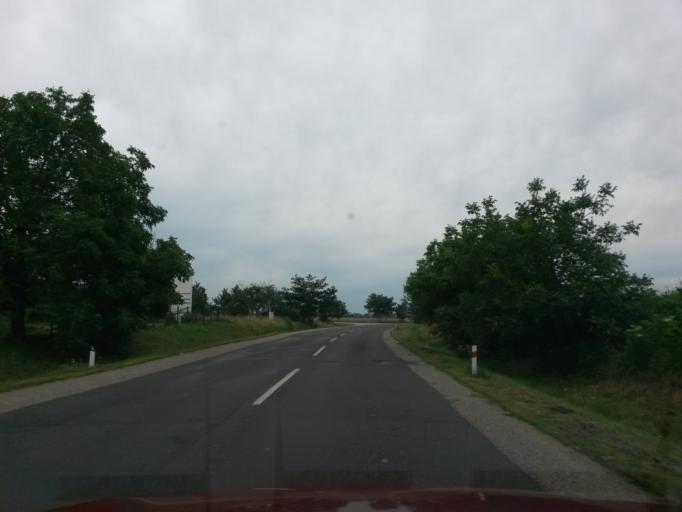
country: SK
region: Nitriansky
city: Surany
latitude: 48.0930
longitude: 18.2914
